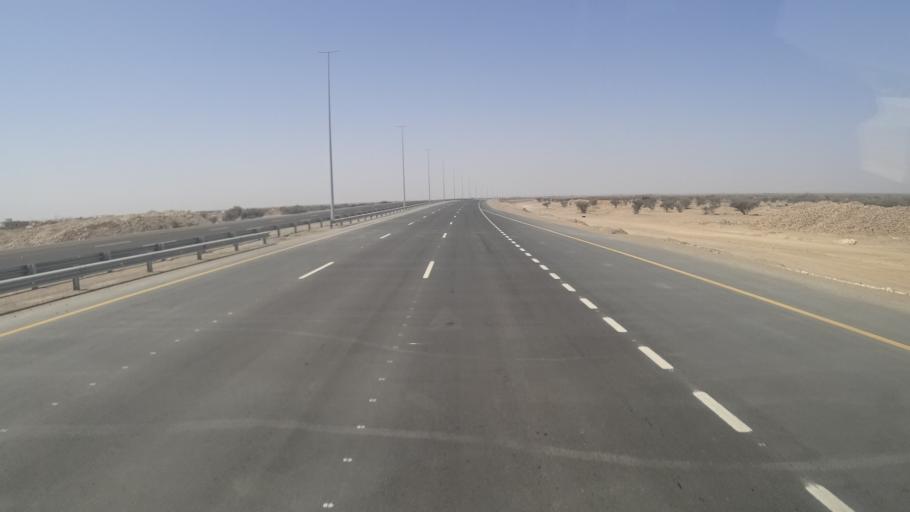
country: OM
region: Ash Sharqiyah
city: Sur
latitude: 22.2760
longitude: 59.2604
